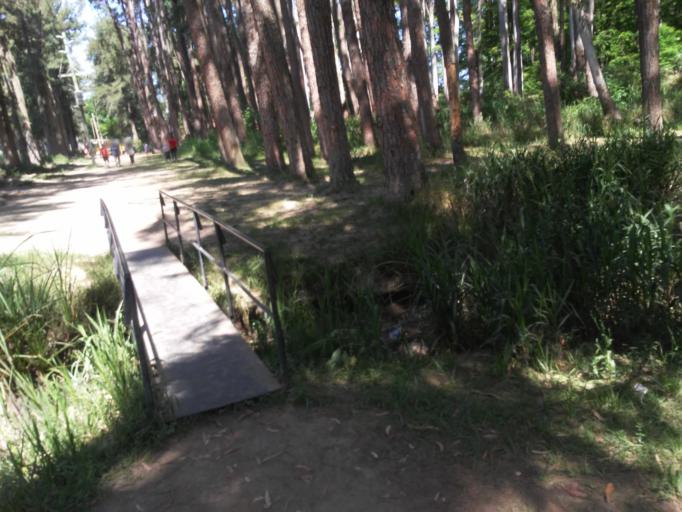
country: AR
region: Buenos Aires
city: Belen de Escobar
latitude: -34.2457
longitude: -58.7386
